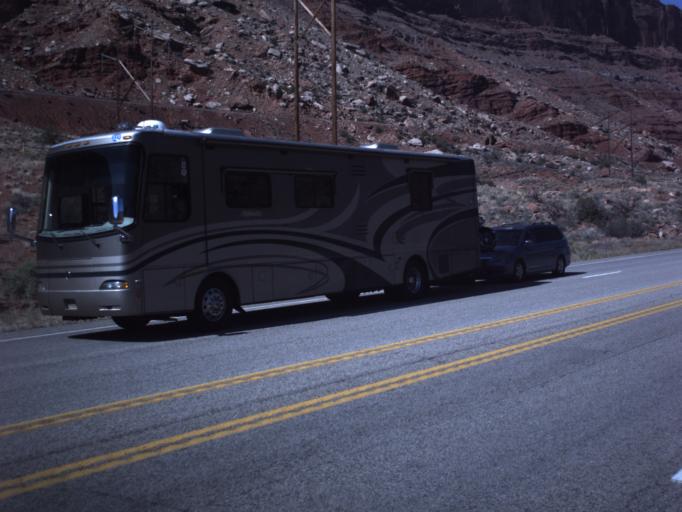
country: US
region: Utah
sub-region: Grand County
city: Moab
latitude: 38.6163
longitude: -109.6314
